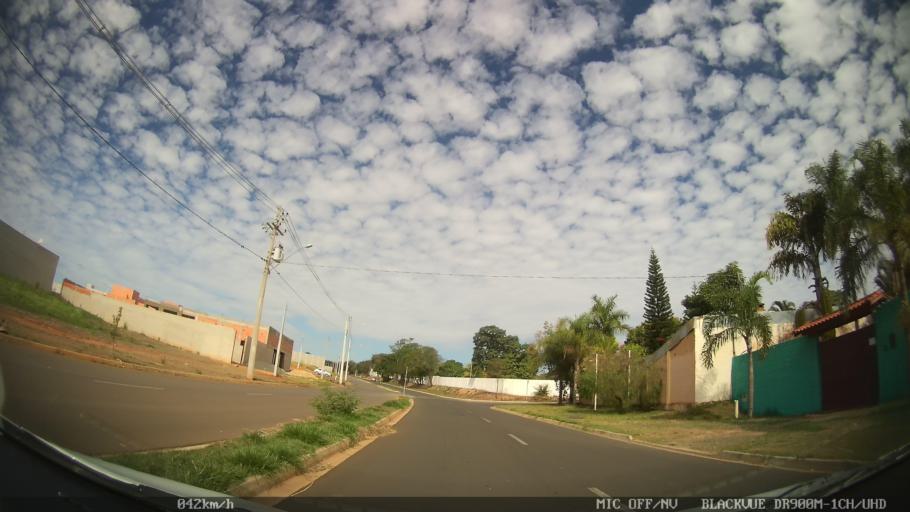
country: BR
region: Sao Paulo
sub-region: Santa Barbara D'Oeste
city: Santa Barbara d'Oeste
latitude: -22.7804
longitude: -47.4031
